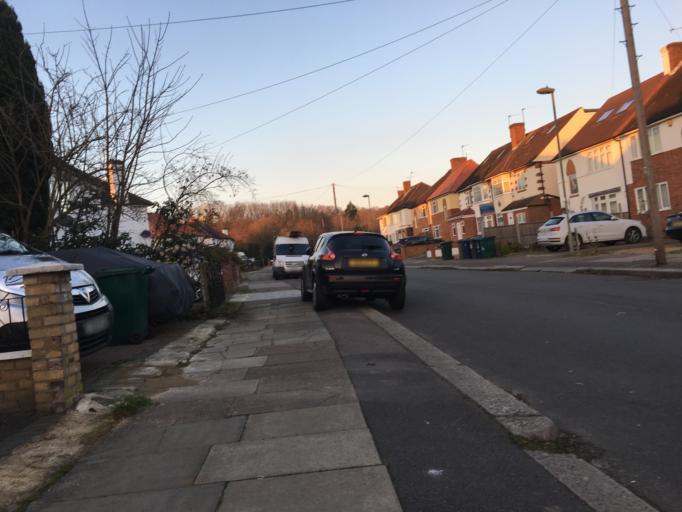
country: GB
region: England
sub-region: Greater London
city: Hendon
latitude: 51.6103
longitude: -0.2259
